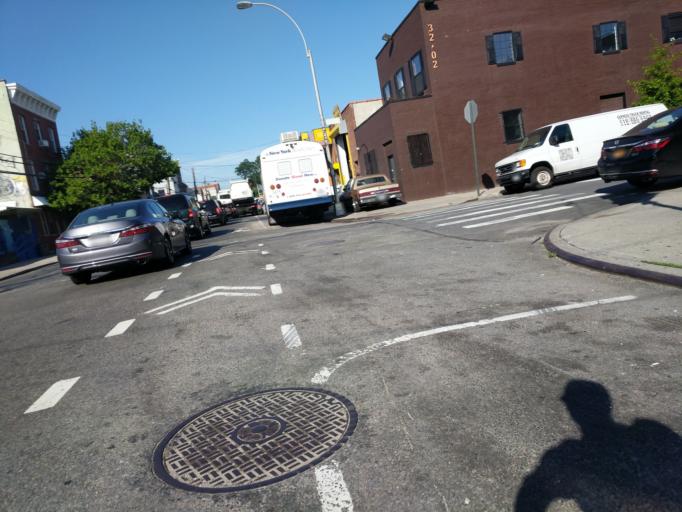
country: US
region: New York
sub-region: Queens County
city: Long Island City
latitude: 40.7348
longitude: -73.9364
